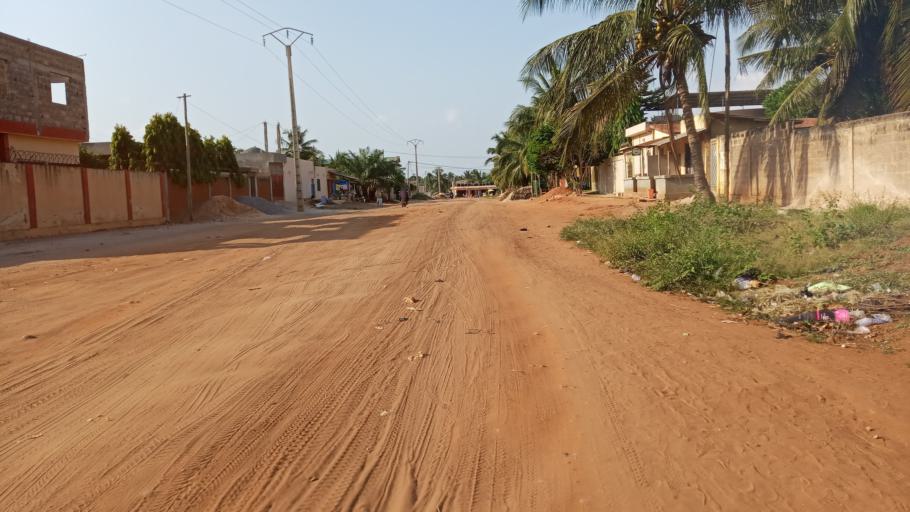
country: TG
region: Maritime
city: Lome
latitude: 6.1774
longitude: 1.1513
